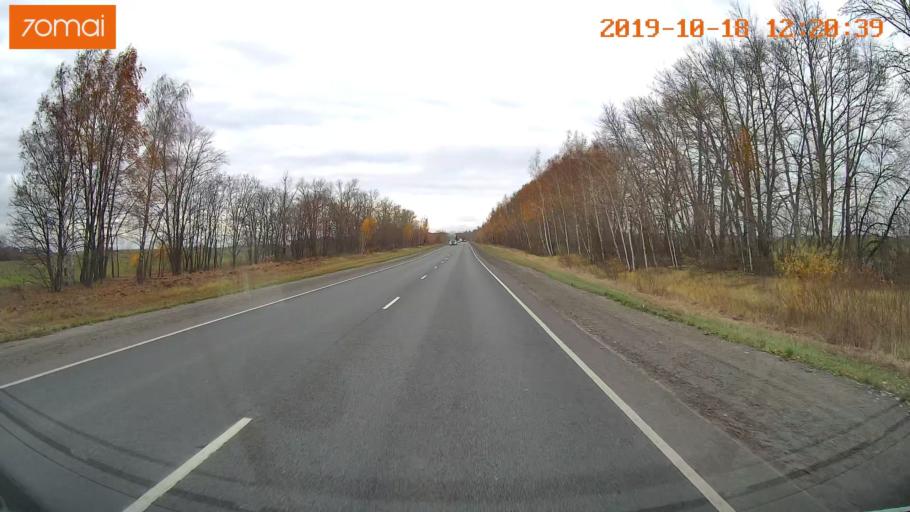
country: RU
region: Rjazan
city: Bagramovo
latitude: 54.5008
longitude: 39.4827
